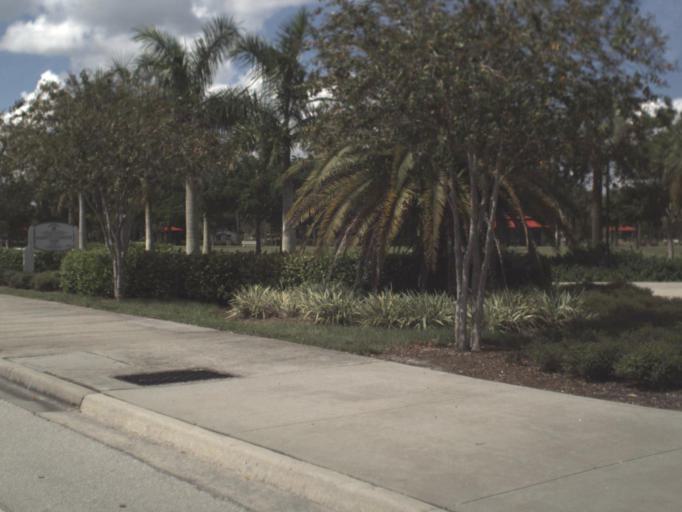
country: US
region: Florida
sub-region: Lee County
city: Fort Myers
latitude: 26.6411
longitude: -81.8467
